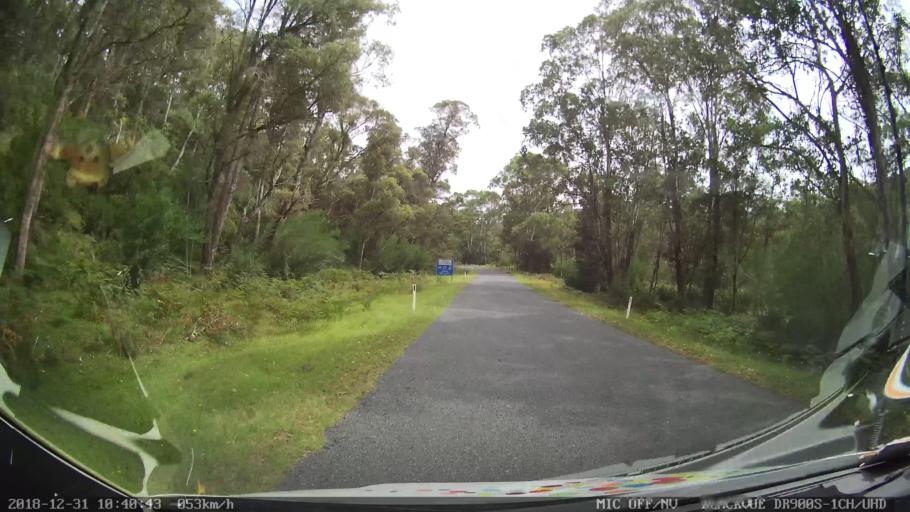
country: AU
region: New South Wales
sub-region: Snowy River
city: Jindabyne
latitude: -36.3893
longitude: 148.1821
